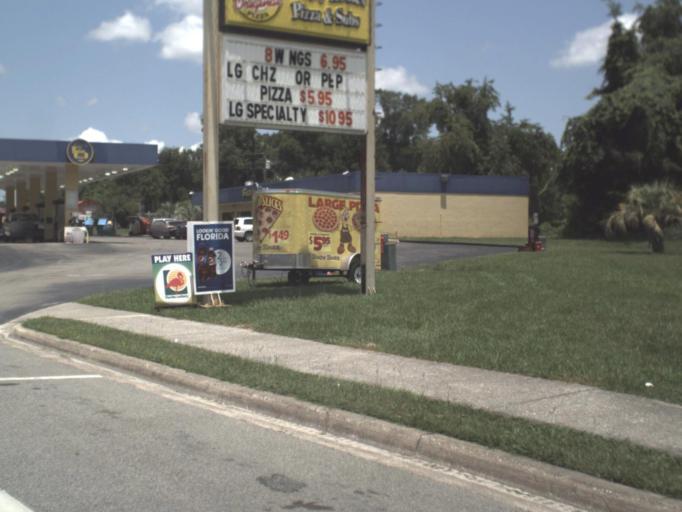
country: US
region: Florida
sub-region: Alachua County
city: High Springs
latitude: 29.9232
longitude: -82.7161
